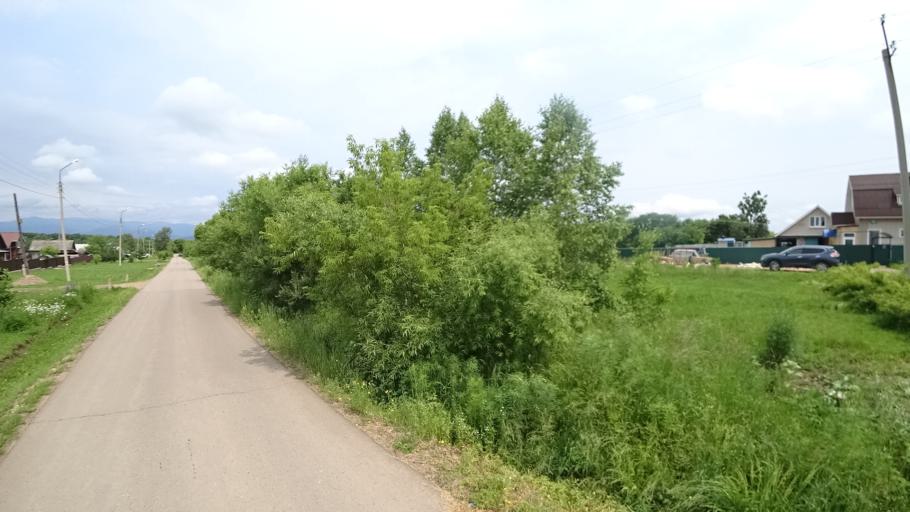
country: RU
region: Primorskiy
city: Novosysoyevka
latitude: 44.2360
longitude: 133.3588
